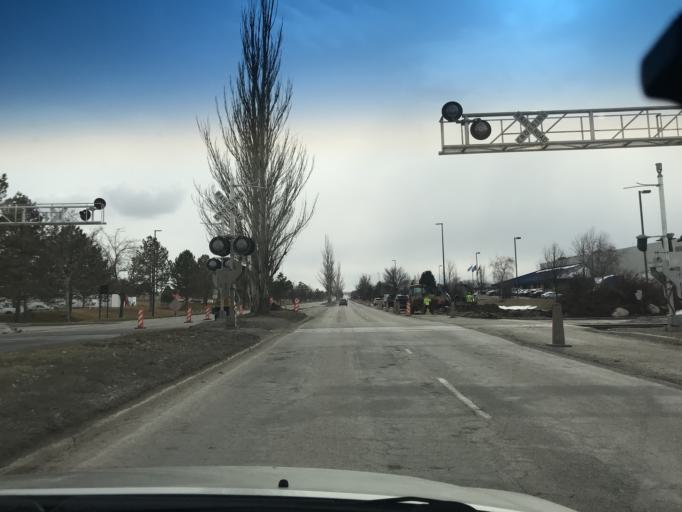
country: US
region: Utah
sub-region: Salt Lake County
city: West Valley City
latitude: 40.7803
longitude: -112.0252
